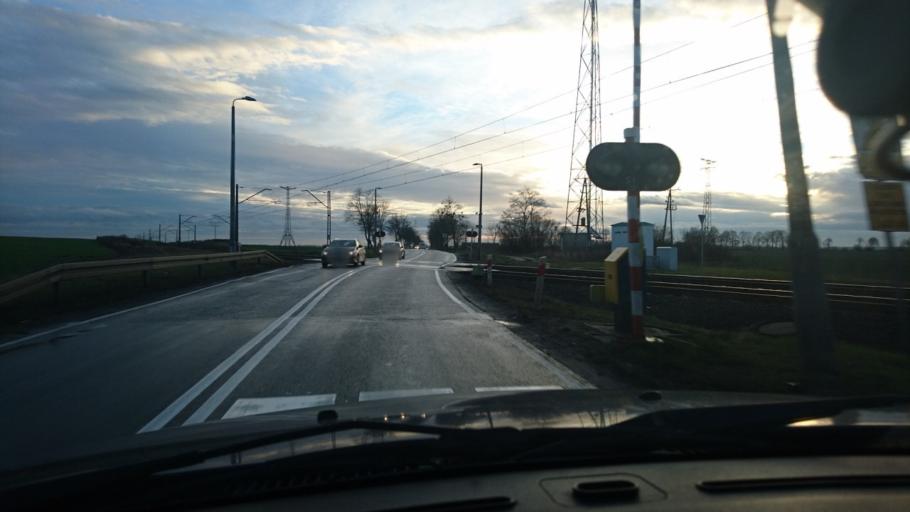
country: PL
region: Opole Voivodeship
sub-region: Powiat kluczborski
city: Byczyna
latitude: 51.0986
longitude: 18.2042
